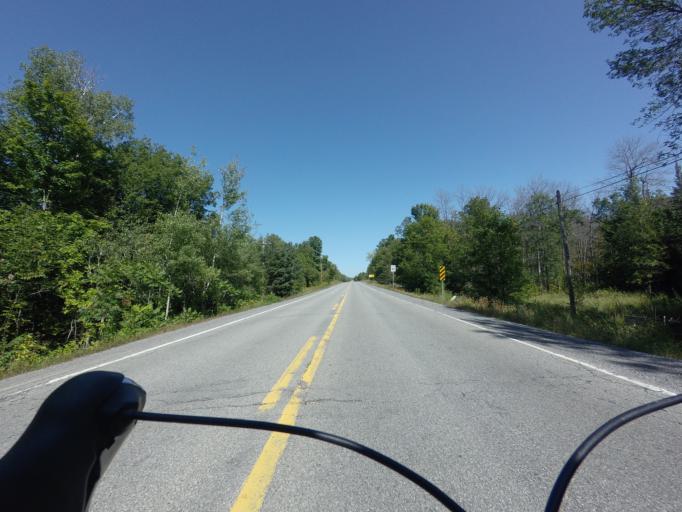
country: CA
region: Ontario
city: Bells Corners
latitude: 45.3843
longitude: -75.9453
